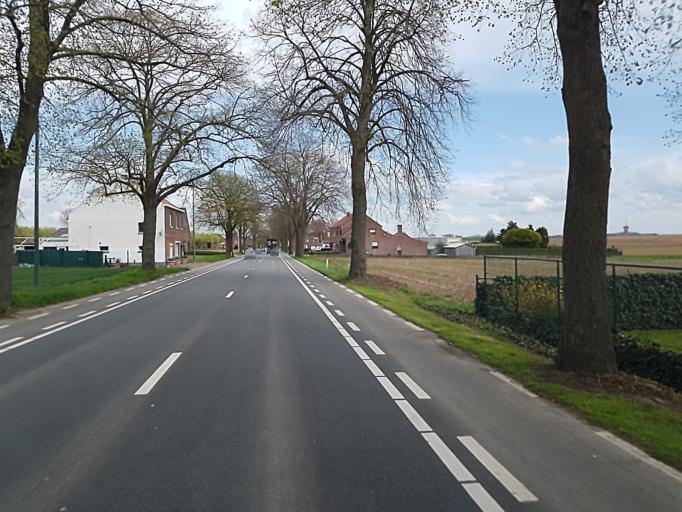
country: BE
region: Flanders
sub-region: Provincie Limburg
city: Riemst
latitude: 50.8165
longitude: 5.6070
